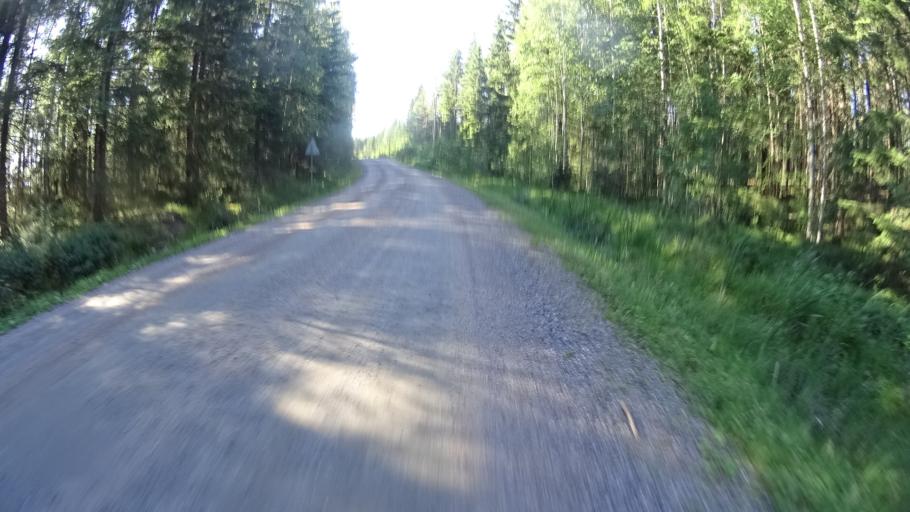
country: FI
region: Uusimaa
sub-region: Helsinki
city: Karkkila
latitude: 60.6495
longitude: 24.1264
